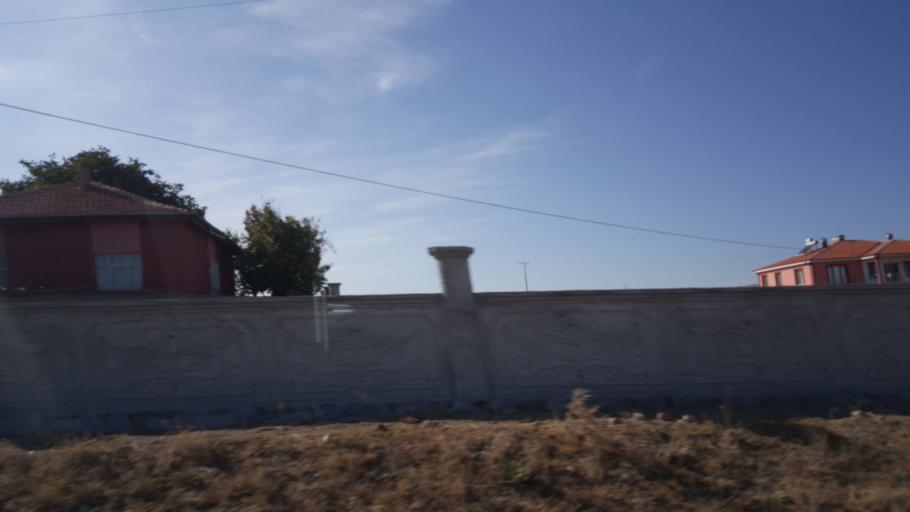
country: TR
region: Ankara
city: Altpinar
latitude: 39.2421
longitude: 32.7431
